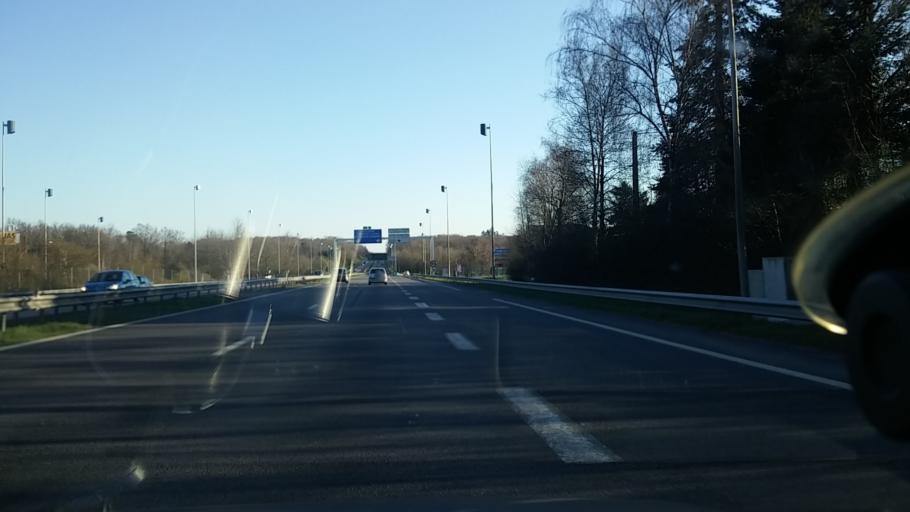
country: FR
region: Limousin
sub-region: Departement de la Haute-Vienne
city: Rilhac-Rancon
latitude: 45.8773
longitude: 1.2878
